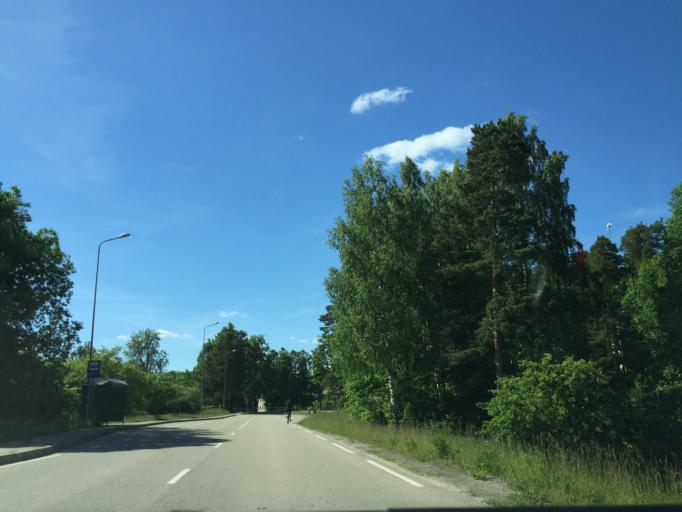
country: LV
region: Preilu Rajons
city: Jaunaglona
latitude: 56.2403
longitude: 27.2172
